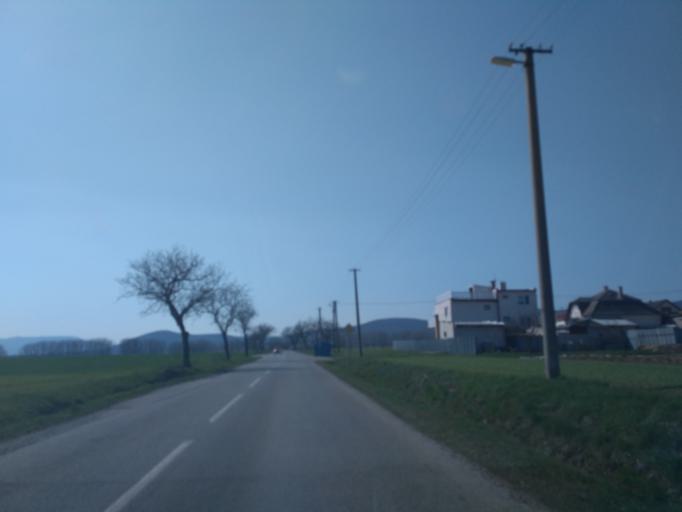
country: SK
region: Kosicky
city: Secovce
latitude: 48.6589
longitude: 21.6077
